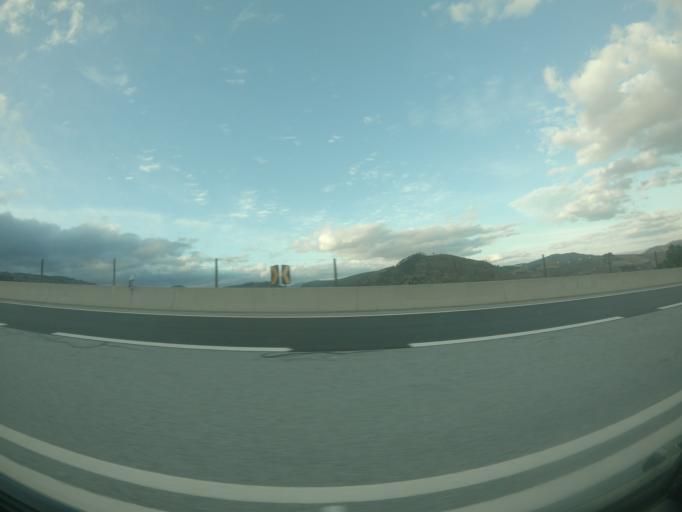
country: PT
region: Vila Real
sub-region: Murca
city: Murca
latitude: 41.3235
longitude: -7.3872
